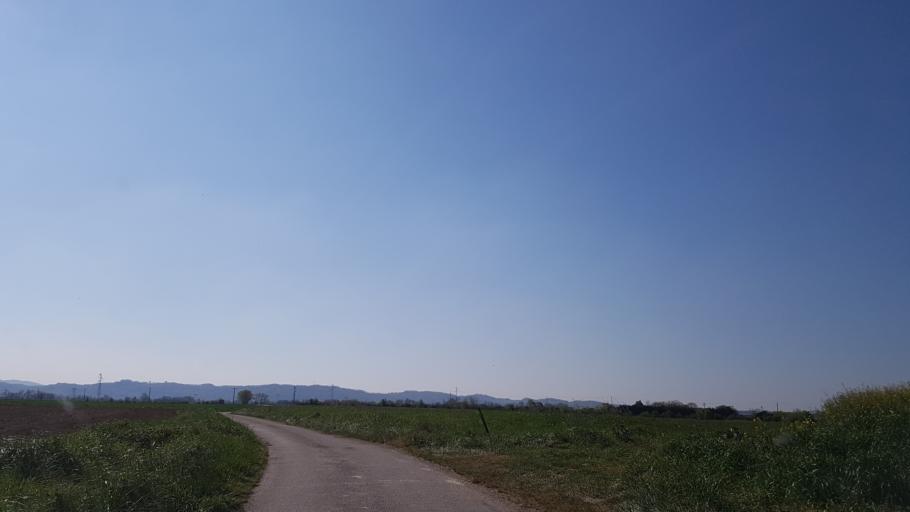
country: FR
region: Midi-Pyrenees
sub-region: Departement de l'Ariege
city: Verniolle
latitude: 43.0867
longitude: 1.6731
